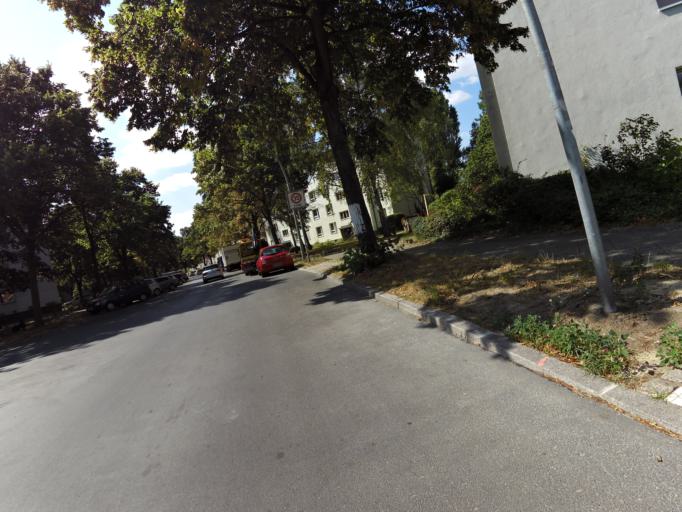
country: DE
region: Berlin
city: Marienfelde
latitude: 52.4271
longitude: 13.3647
